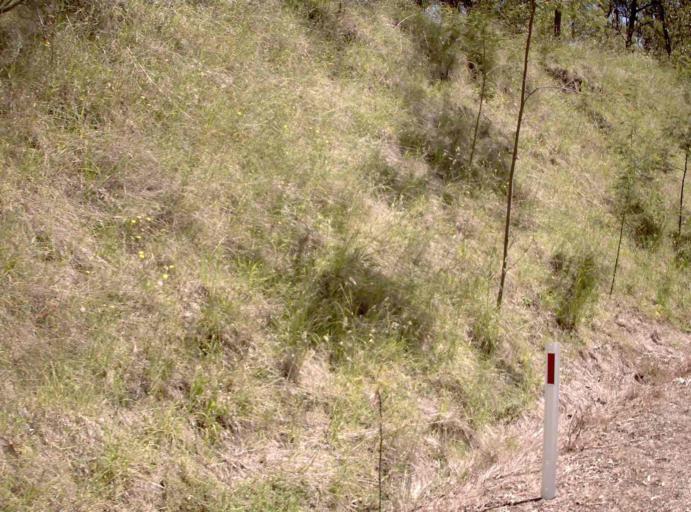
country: AU
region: Victoria
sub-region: East Gippsland
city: Lakes Entrance
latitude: -37.3393
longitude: 148.2287
